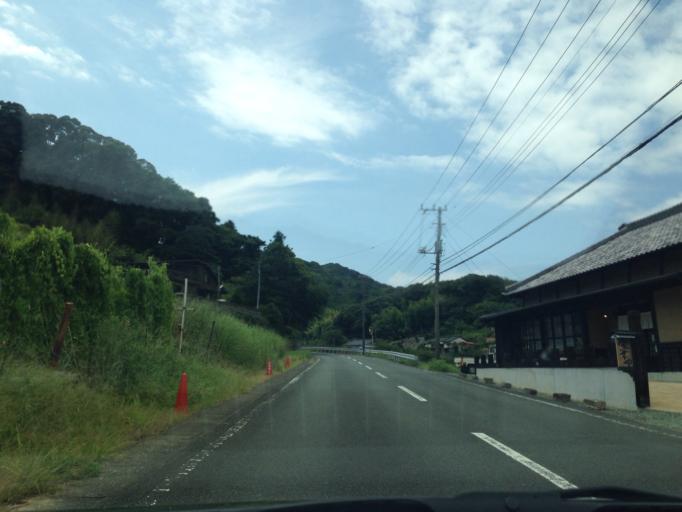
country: JP
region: Shizuoka
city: Shimoda
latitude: 34.6526
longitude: 138.8132
